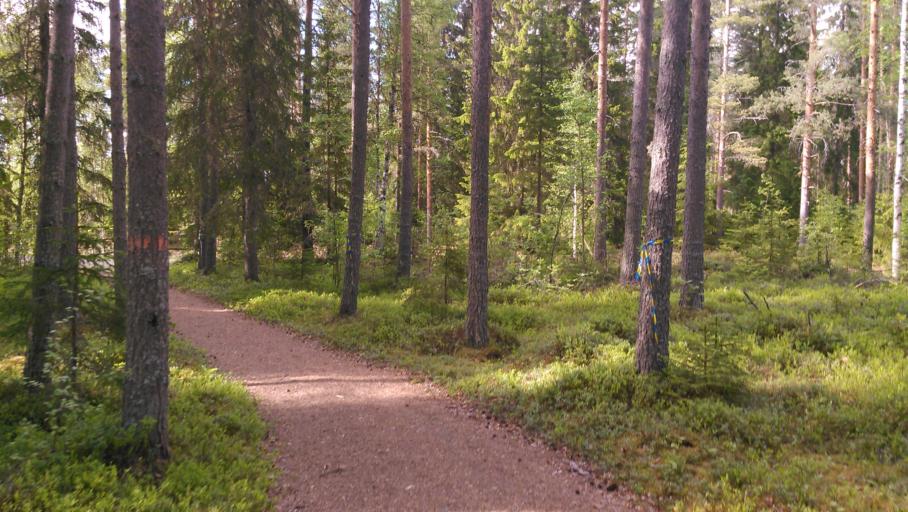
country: SE
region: Vaesterbotten
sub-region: Vannas Kommun
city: Vannasby
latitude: 64.0191
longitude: 19.9034
